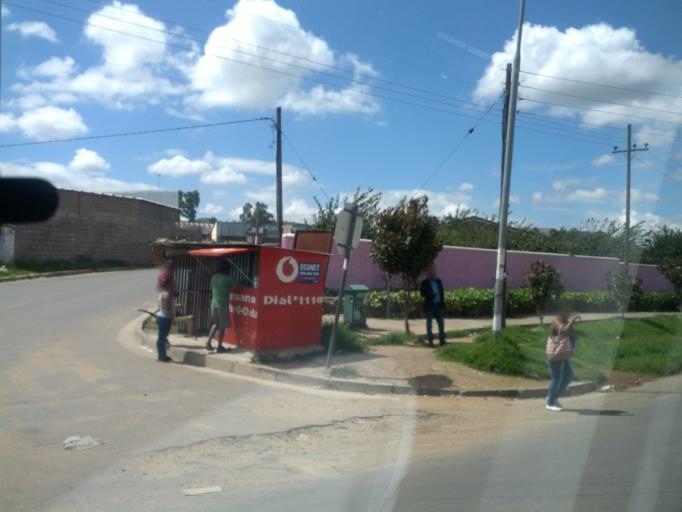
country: LS
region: Maseru
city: Maseru
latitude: -29.2950
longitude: 27.5174
